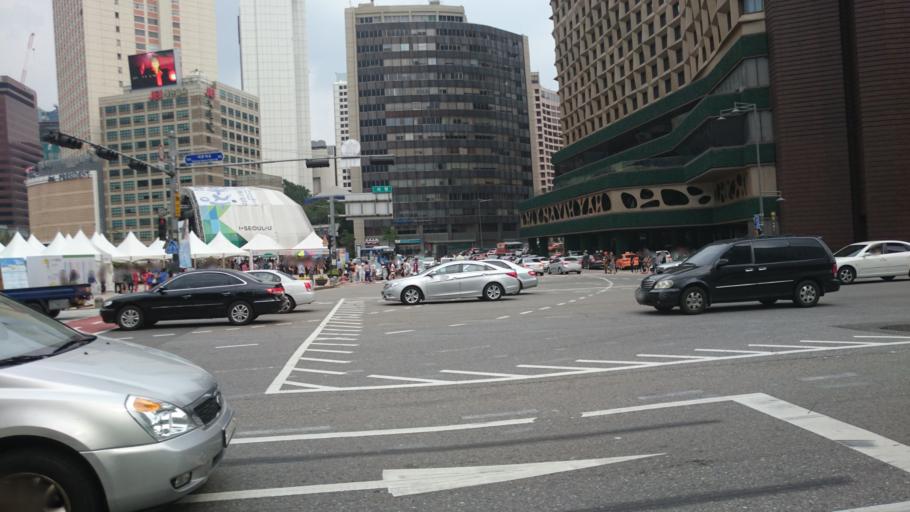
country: KR
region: Seoul
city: Seoul
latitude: 37.5652
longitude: 126.9771
